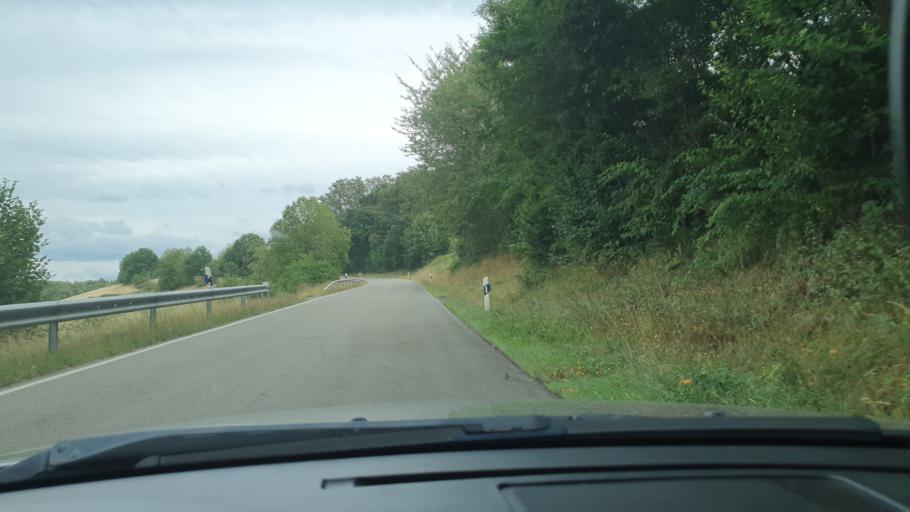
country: DE
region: Rheinland-Pfalz
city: Obernheim-Kirchenarnbach
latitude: 49.3609
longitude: 7.5914
